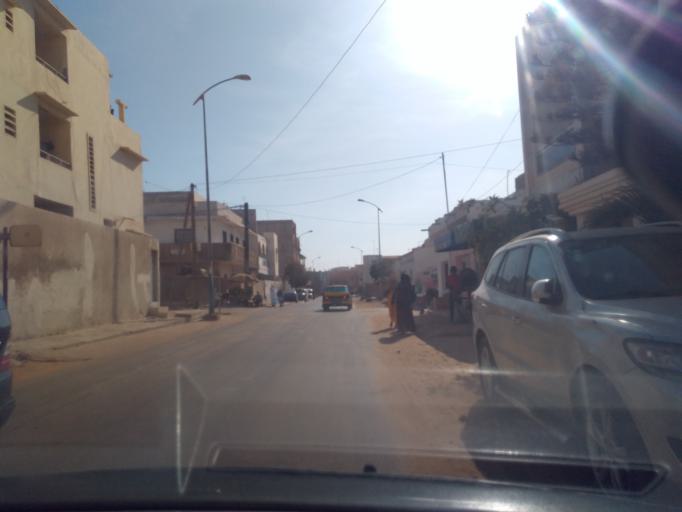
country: SN
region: Dakar
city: Grand Dakar
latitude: 14.7617
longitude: -17.4489
